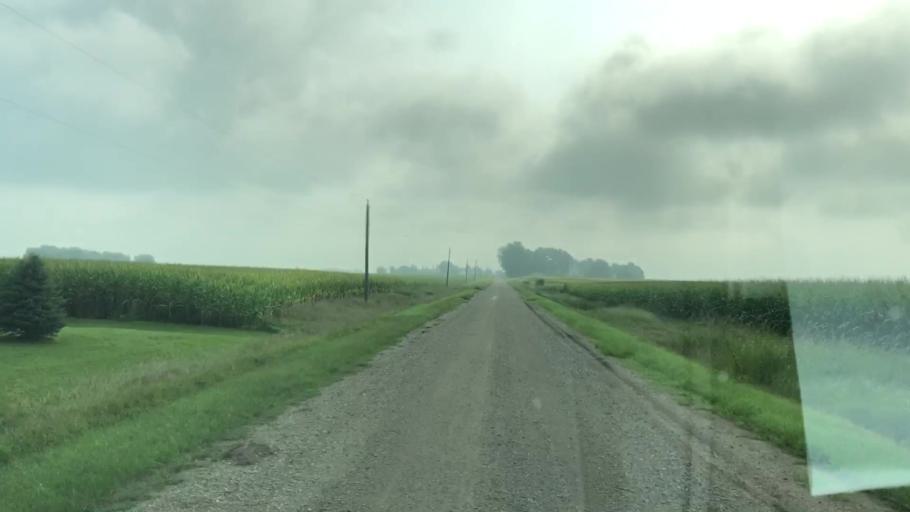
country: US
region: Iowa
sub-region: Sioux County
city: Hull
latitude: 43.2297
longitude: -96.0334
